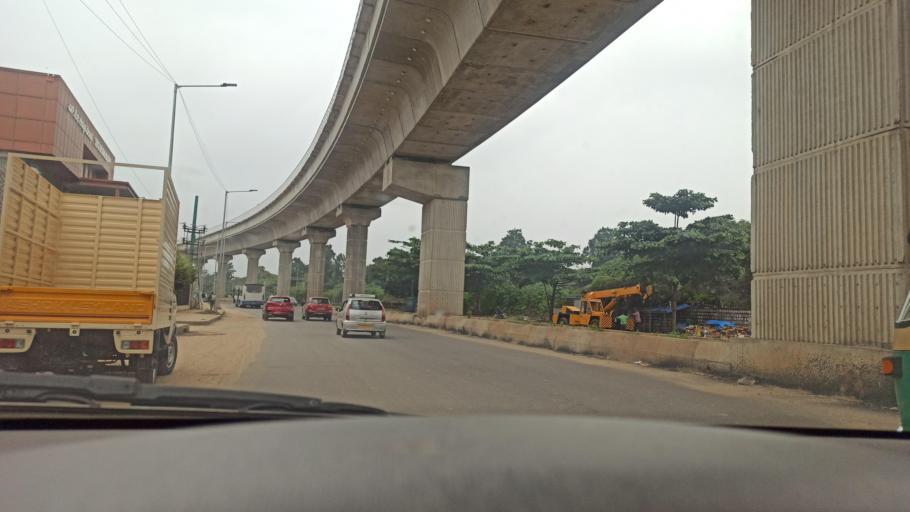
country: IN
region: Karnataka
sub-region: Bangalore Urban
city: Bangalore
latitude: 12.9998
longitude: 77.6869
